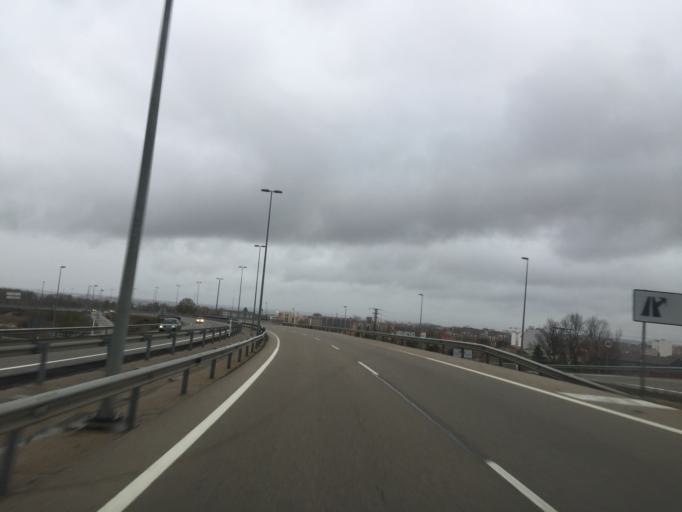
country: ES
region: Castille and Leon
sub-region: Provincia de Leon
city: Leon
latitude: 42.5743
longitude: -5.5509
